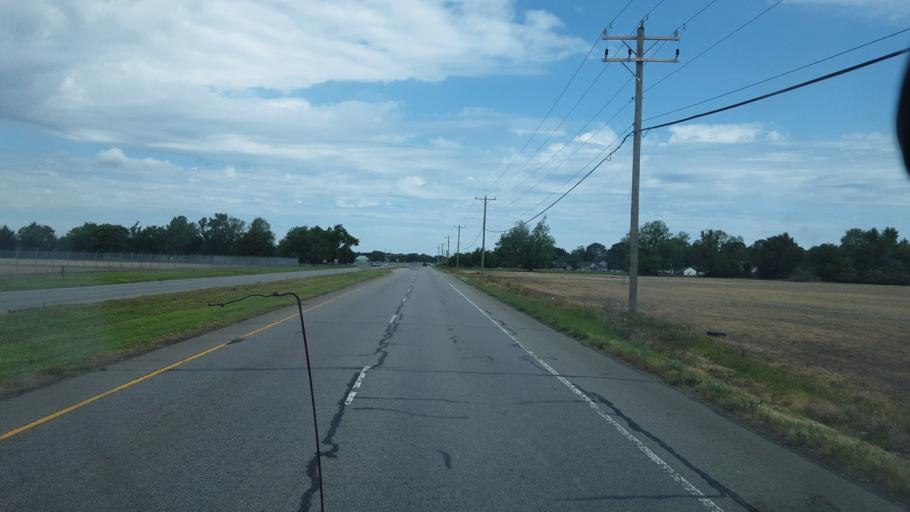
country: US
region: Virginia
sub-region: City of Virginia Beach
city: Virginia Beach
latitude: 36.8149
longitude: -76.0061
